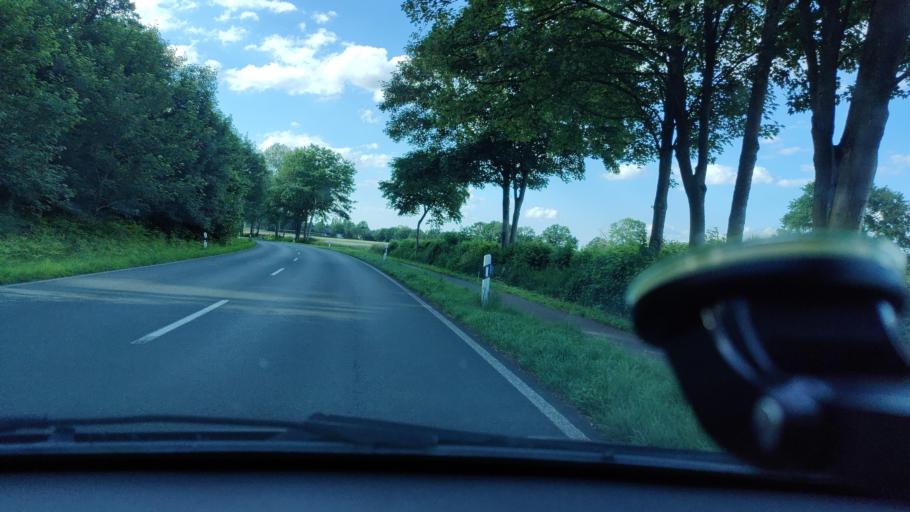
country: DE
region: North Rhine-Westphalia
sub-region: Regierungsbezirk Dusseldorf
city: Alpen
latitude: 51.5653
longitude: 6.5285
